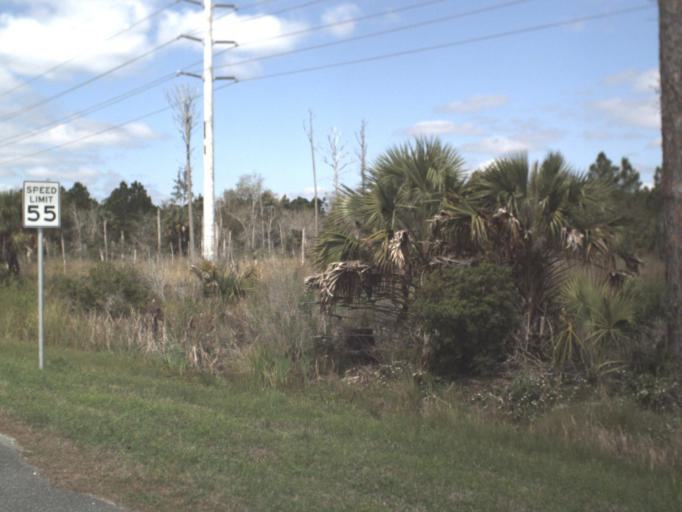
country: US
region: Florida
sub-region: Franklin County
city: Apalachicola
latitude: 29.7144
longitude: -85.0227
